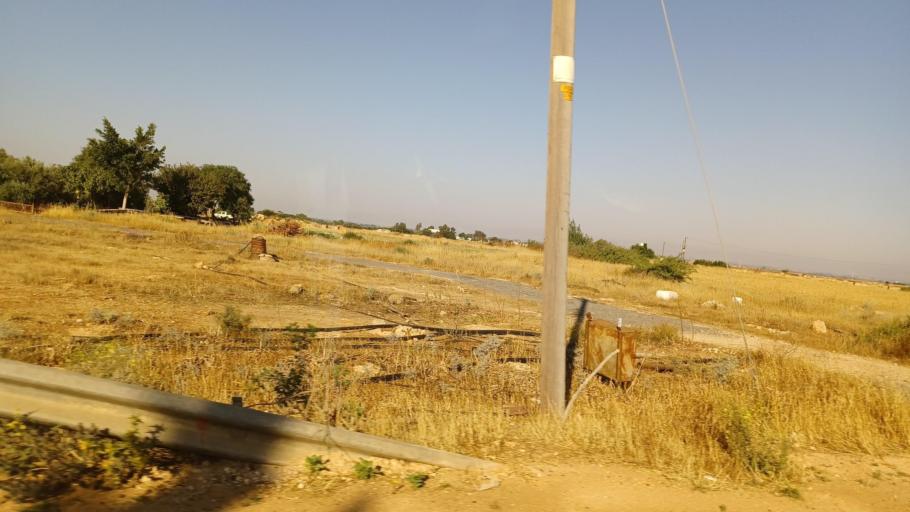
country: CY
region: Ammochostos
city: Frenaros
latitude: 35.0555
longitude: 33.9110
